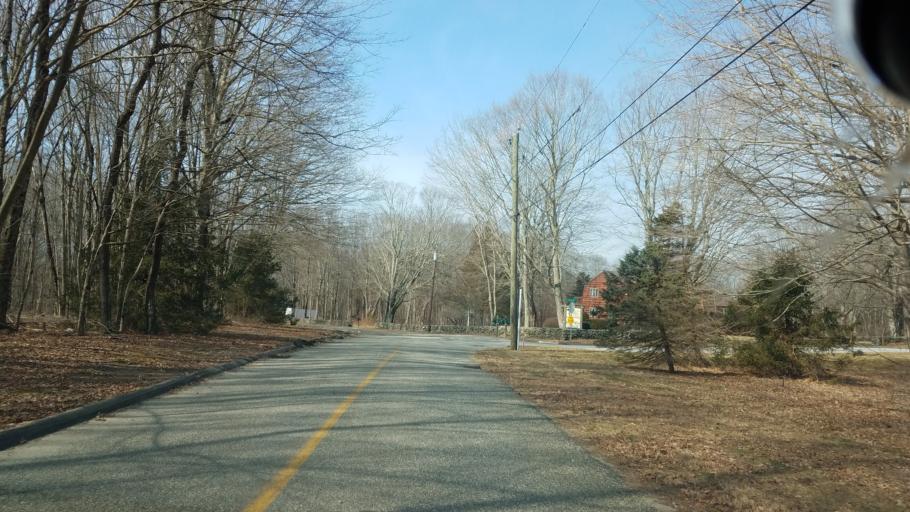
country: US
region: Connecticut
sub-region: New London County
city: Preston City
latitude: 41.5018
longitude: -72.0051
